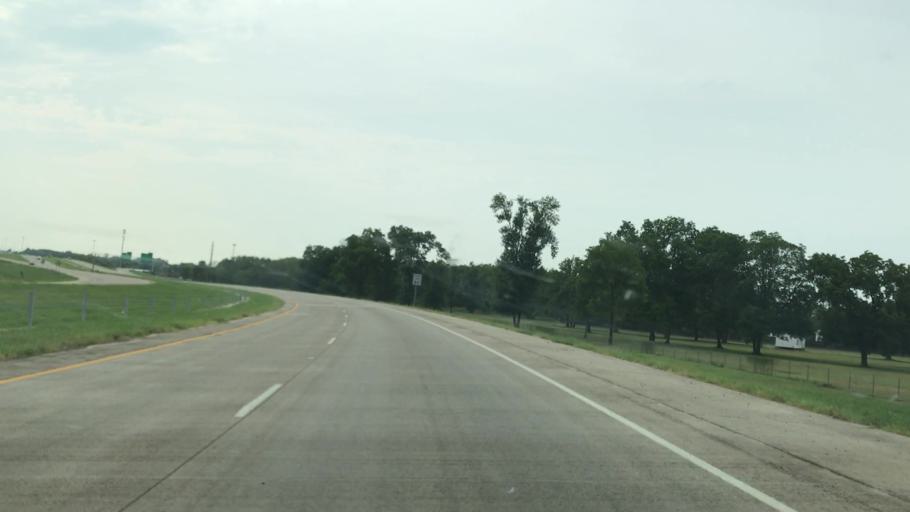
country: US
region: Louisiana
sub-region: Bossier Parish
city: Bossier City
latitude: 32.4082
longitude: -93.7162
